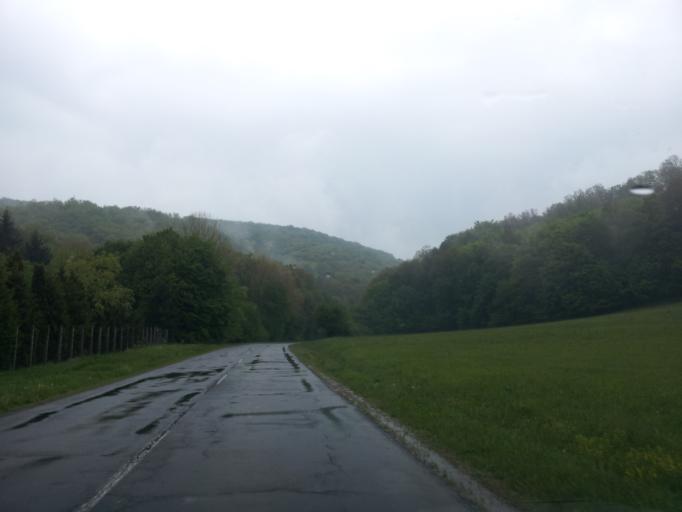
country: HU
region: Baranya
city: Komlo
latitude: 46.2014
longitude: 18.3021
